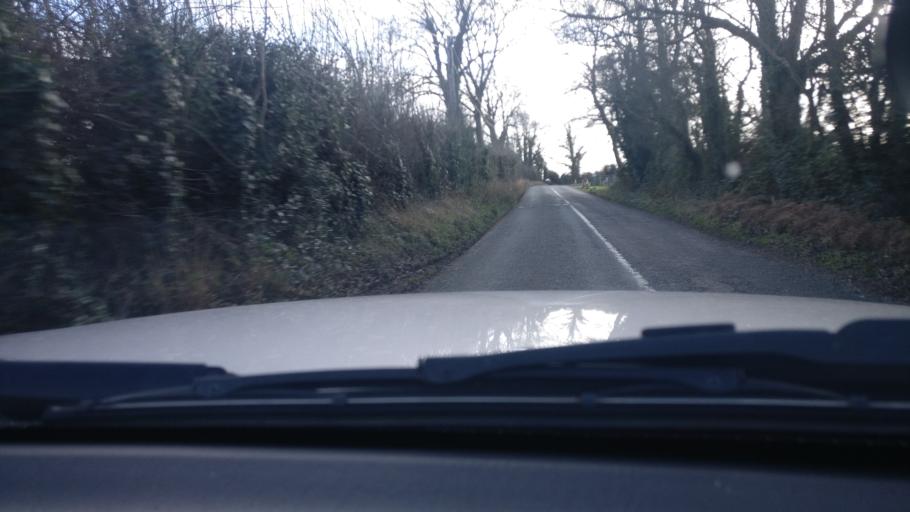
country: IE
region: Connaught
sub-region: County Galway
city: Ballinasloe
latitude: 53.2243
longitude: -8.2915
